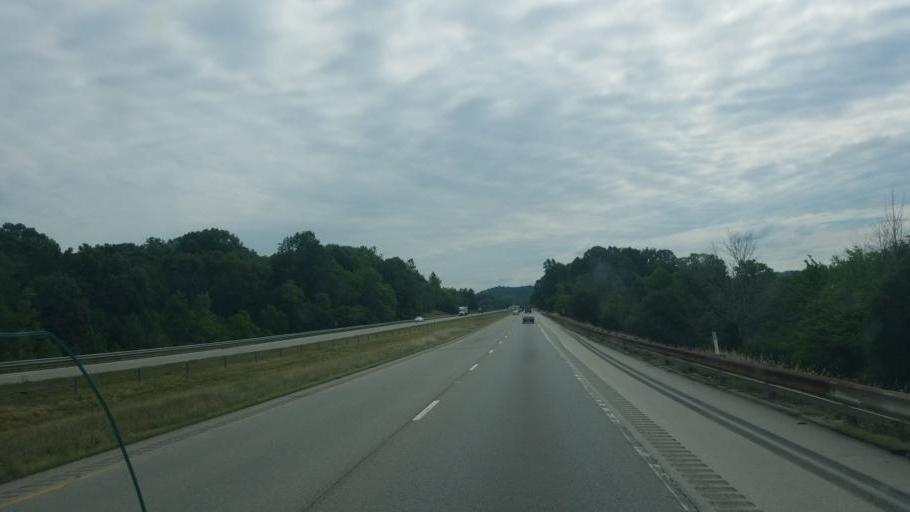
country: US
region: Indiana
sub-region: Clay County
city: Brazil
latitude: 39.5000
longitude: -86.9682
